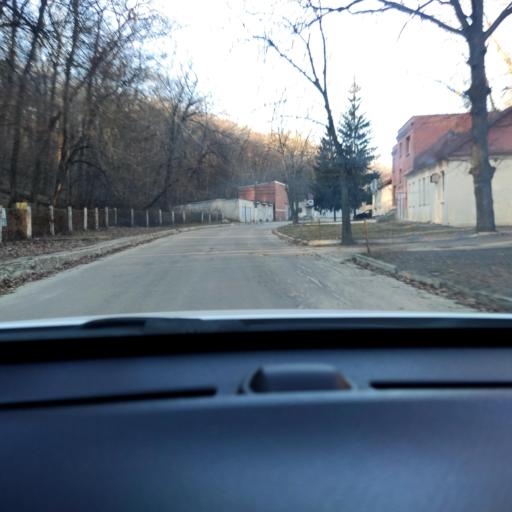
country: RU
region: Voronezj
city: Voronezh
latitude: 51.7265
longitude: 39.2309
